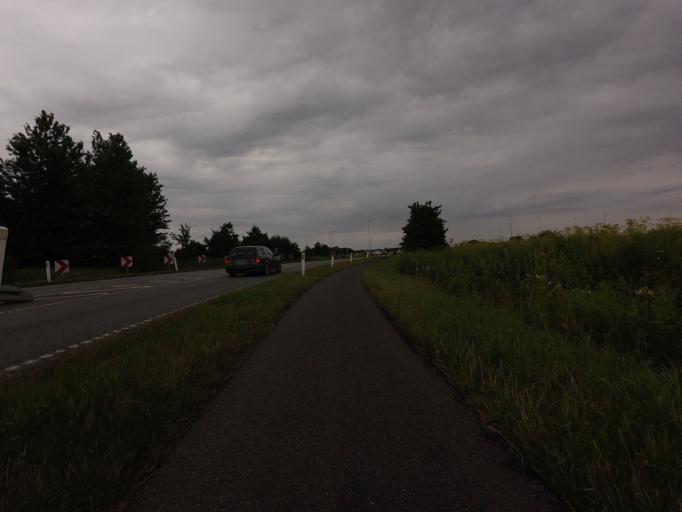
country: DK
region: North Denmark
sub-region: Alborg Kommune
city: Vadum
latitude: 57.1010
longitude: 9.8850
